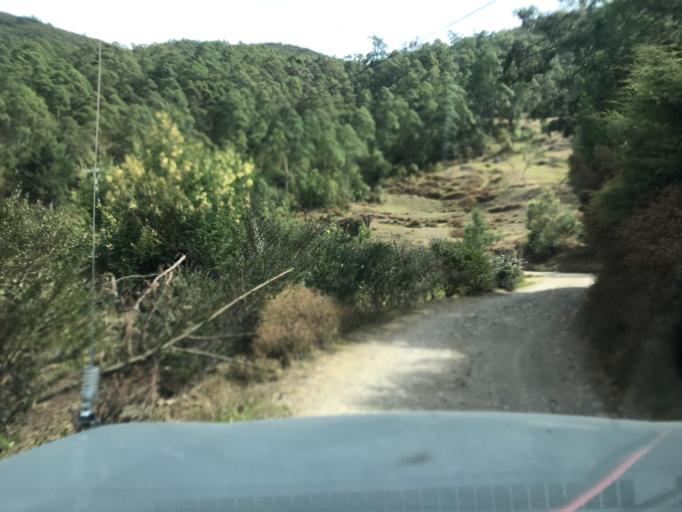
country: TL
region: Ainaro
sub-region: Ainaro
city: Ainaro
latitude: -8.8826
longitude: 125.5430
